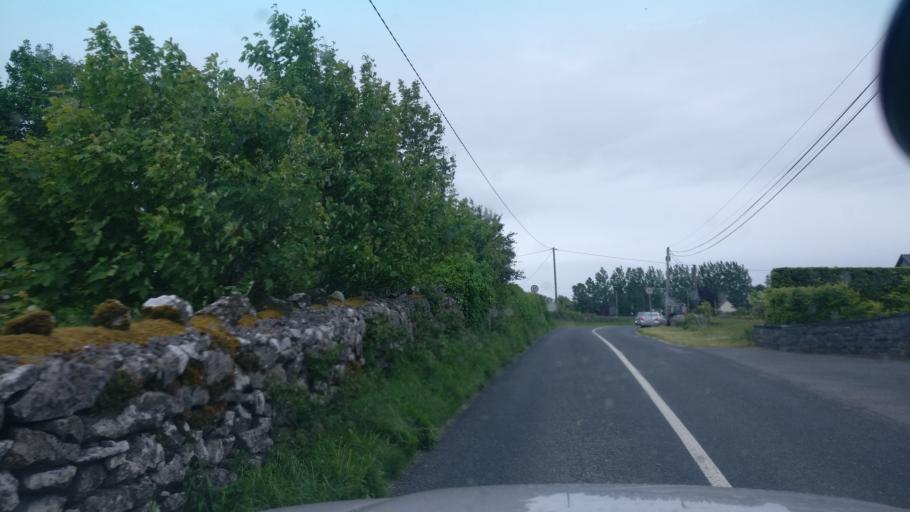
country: IE
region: Connaught
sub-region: County Galway
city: Gort
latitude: 53.0639
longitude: -8.7669
